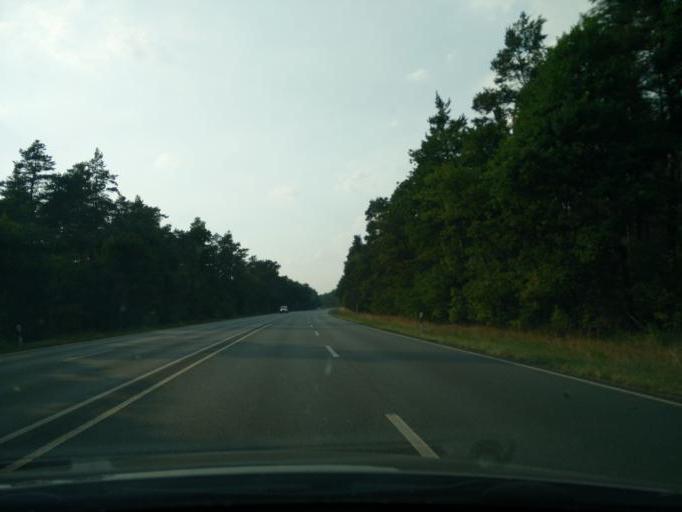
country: DE
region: Bavaria
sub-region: Regierungsbezirk Mittelfranken
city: Schwaig
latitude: 49.4249
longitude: 11.1492
